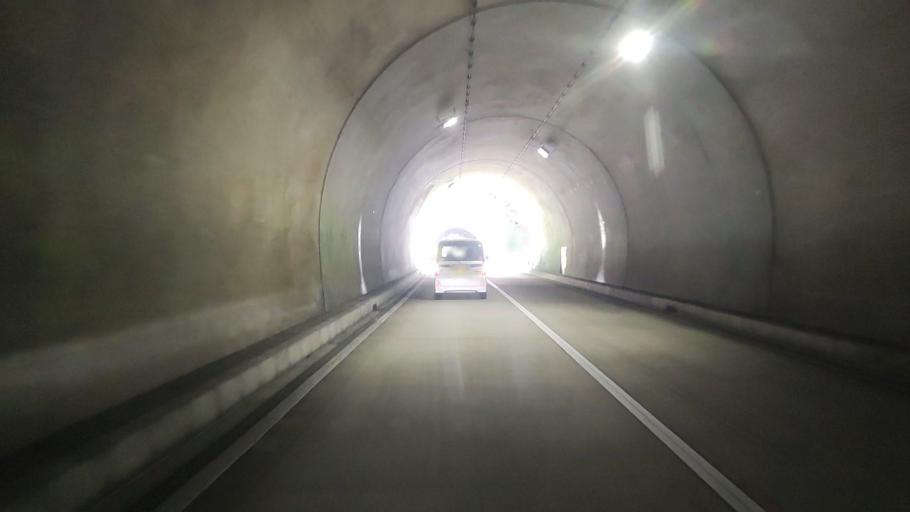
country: JP
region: Wakayama
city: Shingu
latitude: 33.8886
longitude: 135.8797
